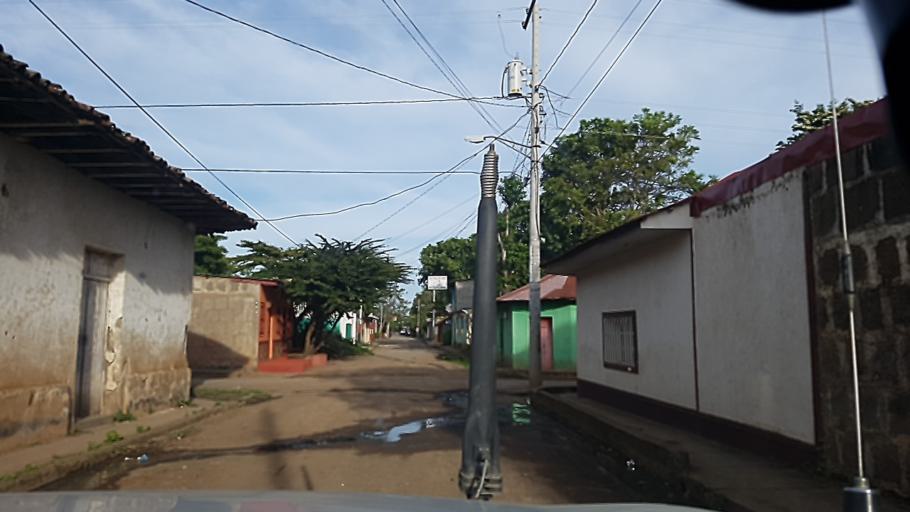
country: NI
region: Carazo
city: La Paz de Oriente
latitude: 11.8049
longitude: -86.1643
